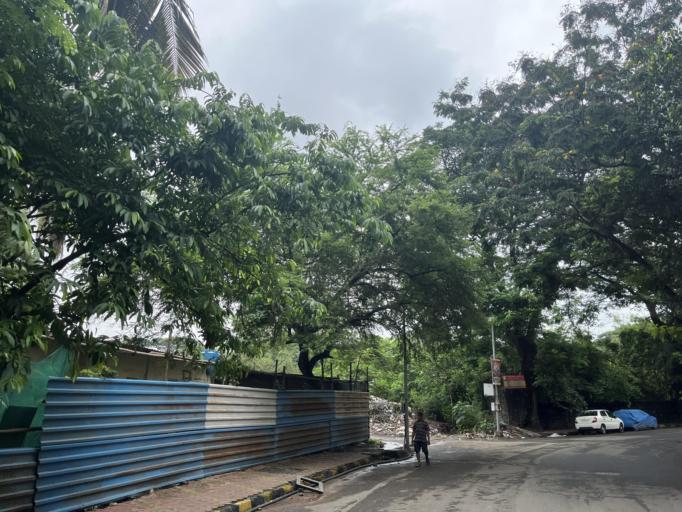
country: IN
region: Maharashtra
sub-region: Mumbai Suburban
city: Borivli
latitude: 19.2318
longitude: 72.8666
